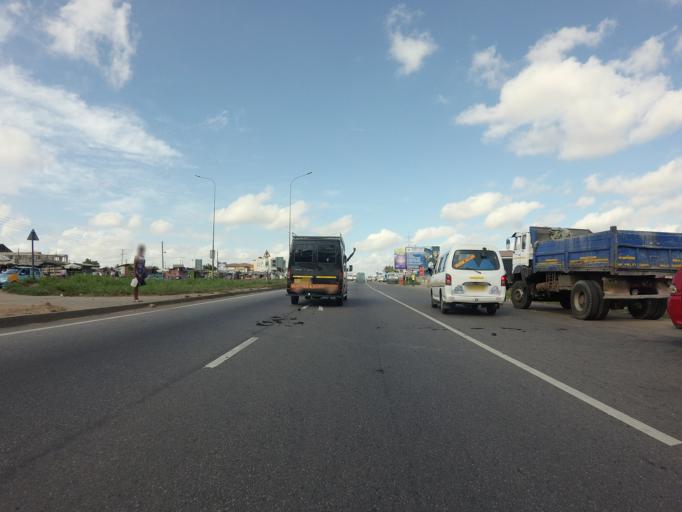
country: GH
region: Central
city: Kasoa
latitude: 5.5386
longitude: -0.4001
